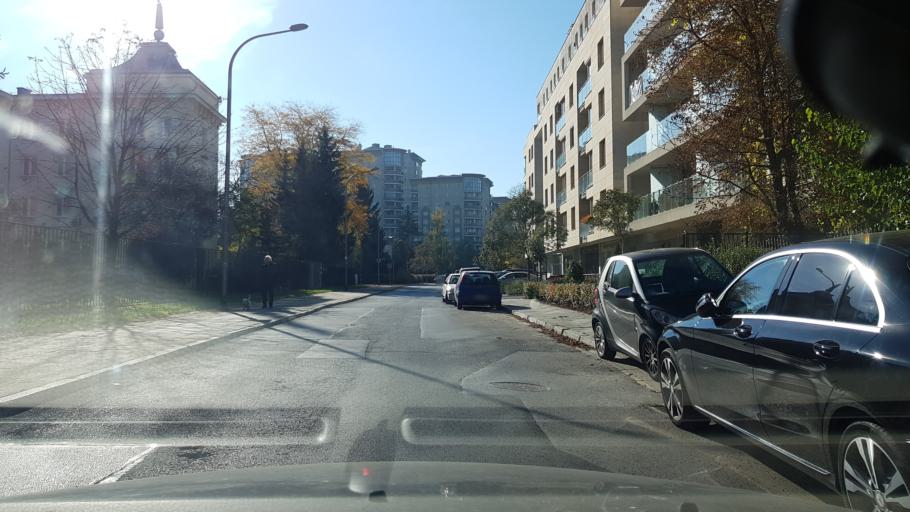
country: PL
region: Masovian Voivodeship
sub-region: Warszawa
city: Mokotow
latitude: 52.1882
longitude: 21.0219
